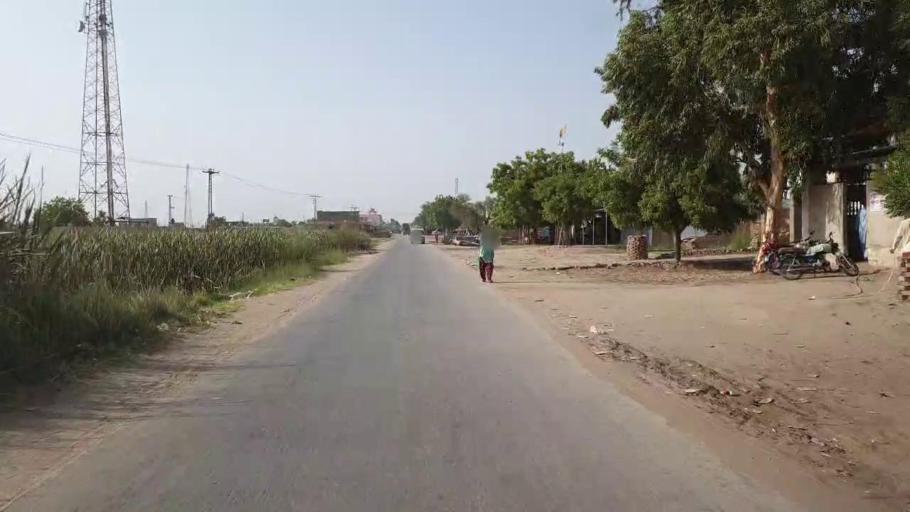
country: PK
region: Sindh
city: Sanghar
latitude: 26.2673
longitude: 68.9295
